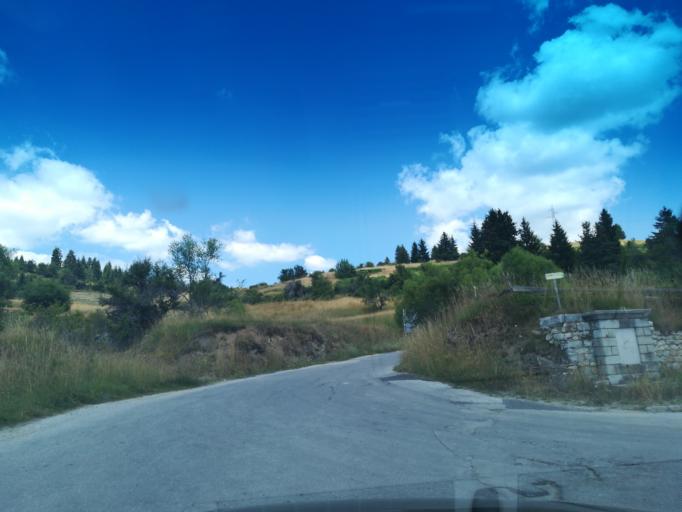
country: BG
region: Smolyan
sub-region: Obshtina Chepelare
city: Chepelare
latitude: 41.6719
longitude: 24.7760
